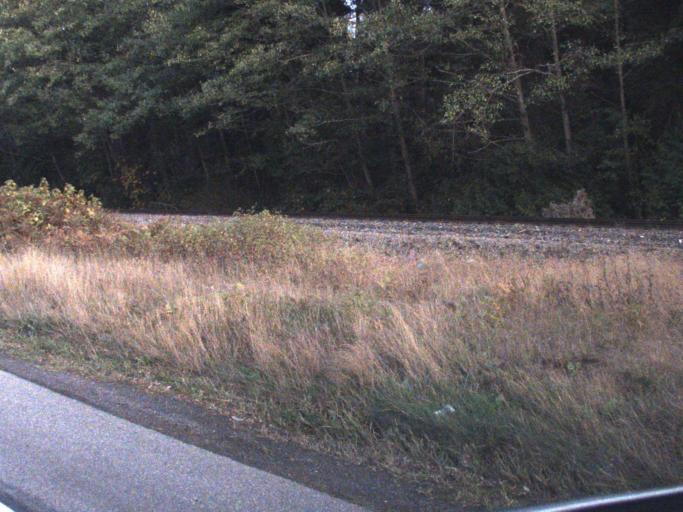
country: US
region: Washington
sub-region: Skagit County
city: Sedro-Woolley
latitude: 48.4957
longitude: -122.2718
